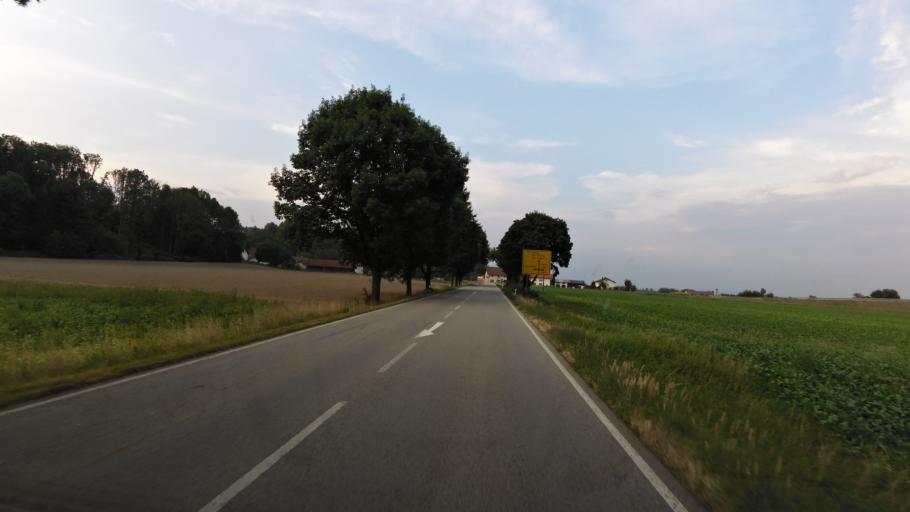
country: DE
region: Bavaria
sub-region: Lower Bavaria
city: Rotthalmunster
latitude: 48.3324
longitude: 13.2251
